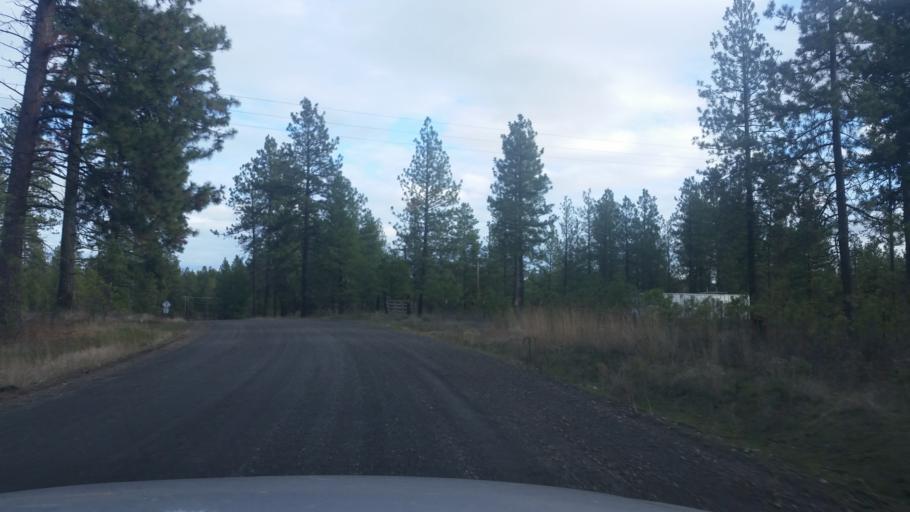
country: US
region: Washington
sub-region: Spokane County
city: Cheney
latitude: 47.4347
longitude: -117.4401
